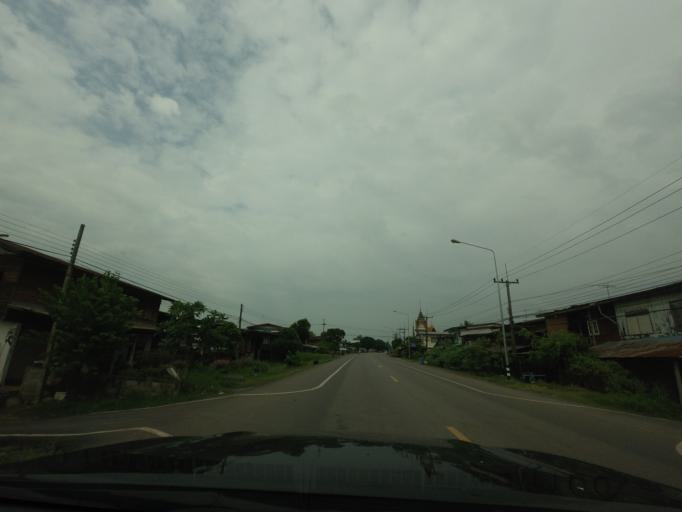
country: TH
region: Nong Khai
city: Tha Bo
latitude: 17.7997
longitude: 102.6689
